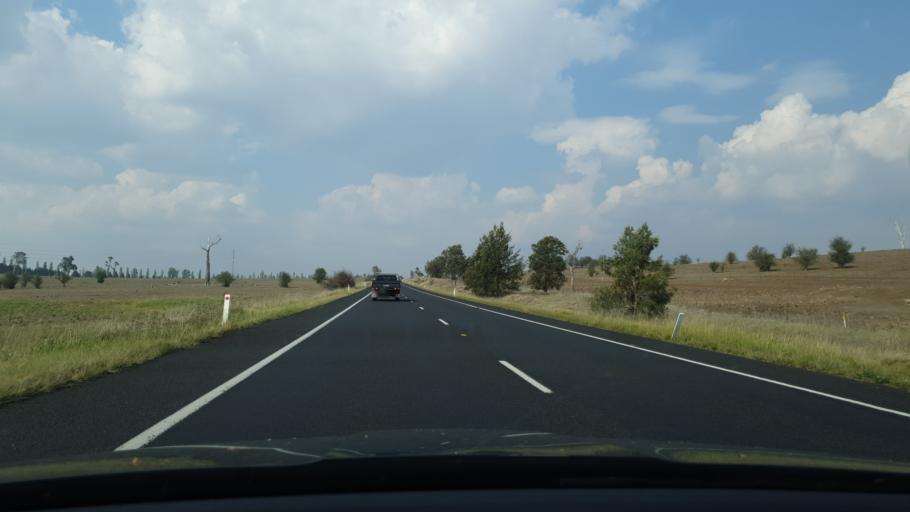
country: AU
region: New South Wales
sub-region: Glen Innes Severn
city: Glen Innes
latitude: -29.6991
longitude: 151.7471
